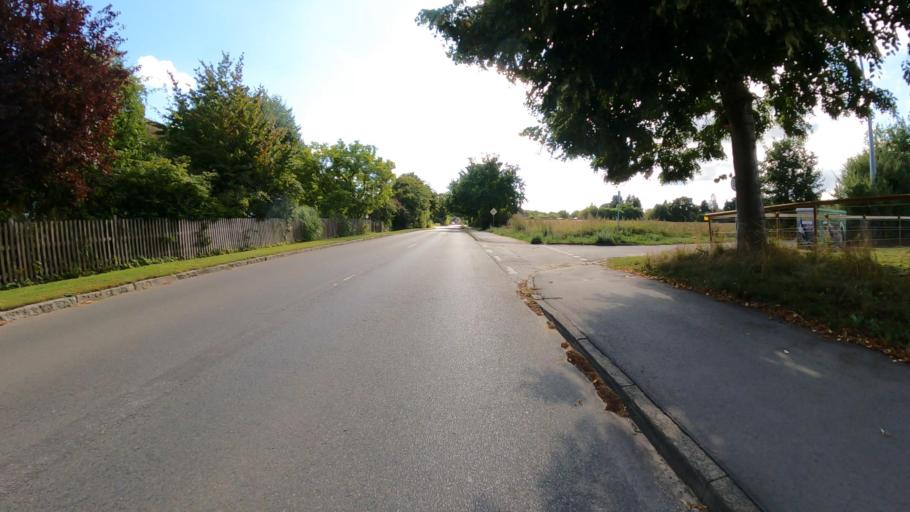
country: DE
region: Schleswig-Holstein
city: Hoisdorf
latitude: 53.6736
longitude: 10.3303
